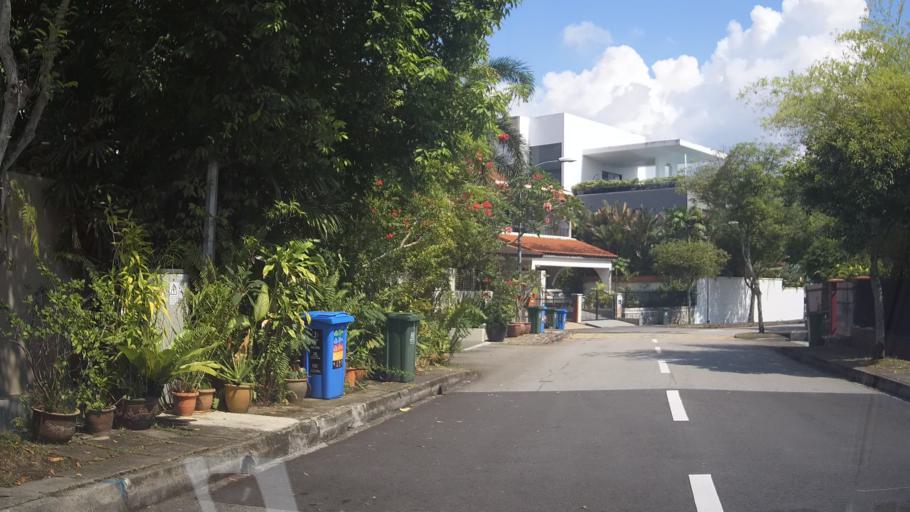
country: MY
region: Johor
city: Kampung Pasir Gudang Baru
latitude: 1.3815
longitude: 103.9465
